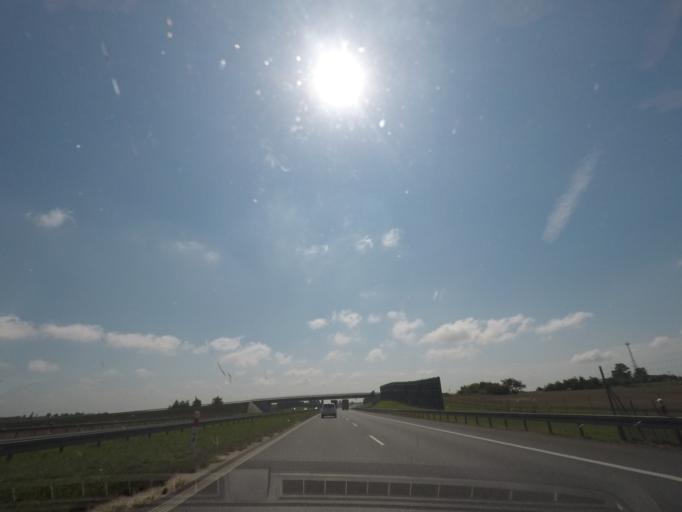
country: PL
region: Kujawsko-Pomorskie
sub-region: Powiat wloclawski
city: Kowal
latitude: 52.4774
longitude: 19.1743
